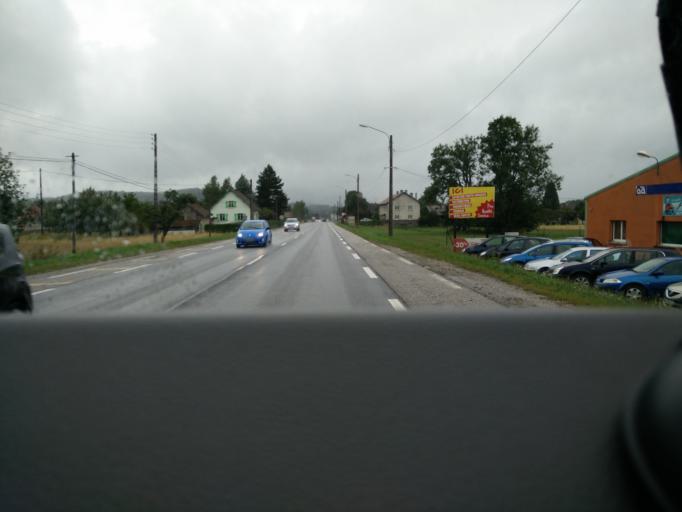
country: FR
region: Lorraine
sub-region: Departement des Vosges
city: Saint-Leonard
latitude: 48.2029
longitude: 6.9449
